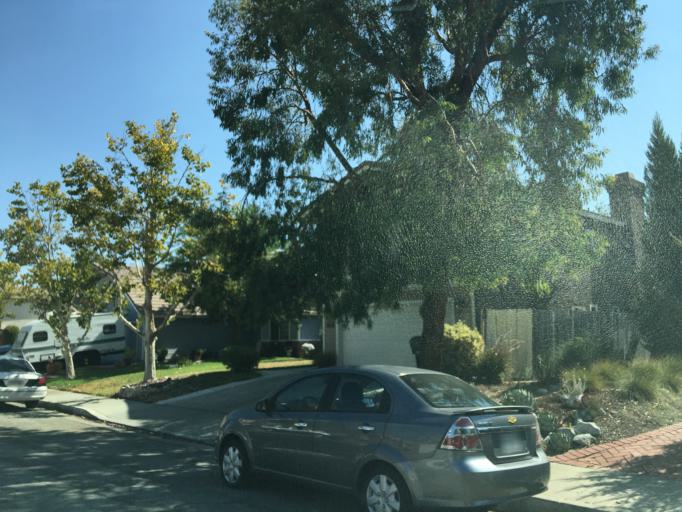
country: US
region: California
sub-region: Los Angeles County
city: Valencia
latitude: 34.4473
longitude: -118.6210
